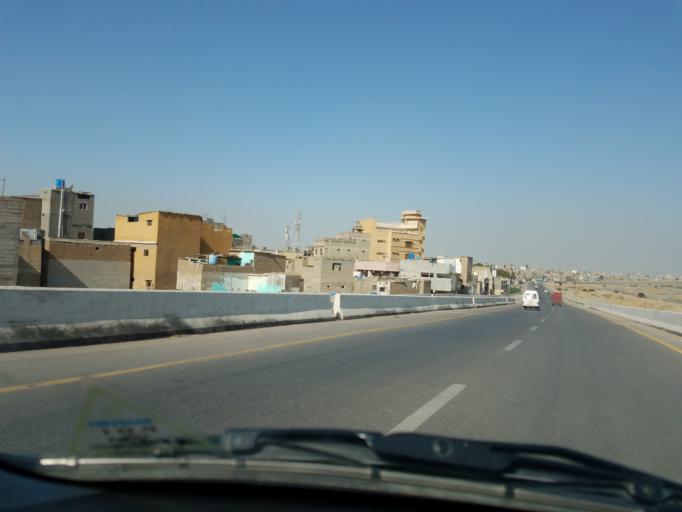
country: PK
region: Sindh
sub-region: Karachi District
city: Karachi
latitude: 24.8853
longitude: 67.0221
